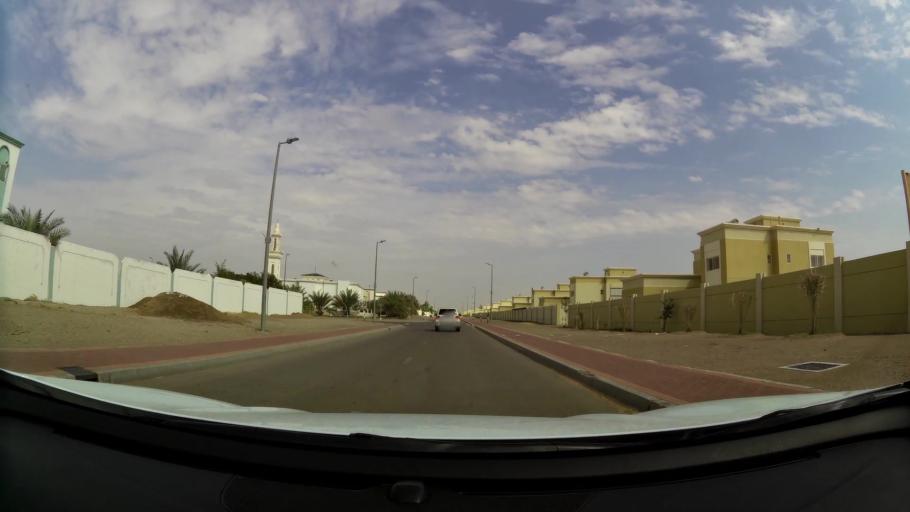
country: AE
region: Abu Dhabi
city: Al Ain
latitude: 24.0947
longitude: 55.8947
